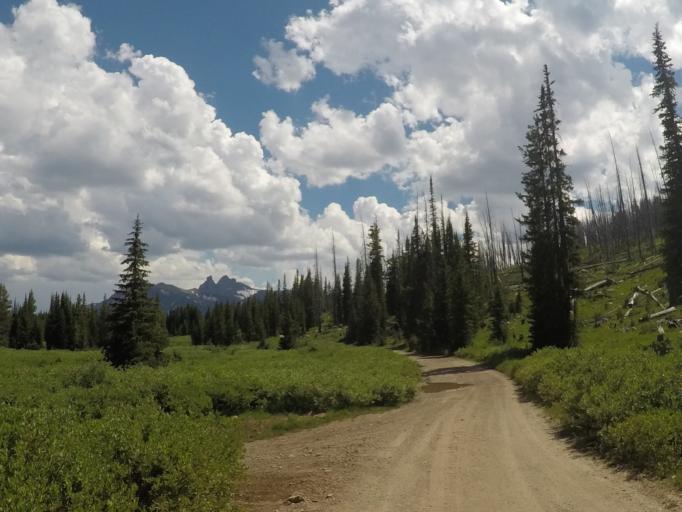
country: US
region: Montana
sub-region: Stillwater County
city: Absarokee
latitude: 45.0385
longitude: -109.9078
